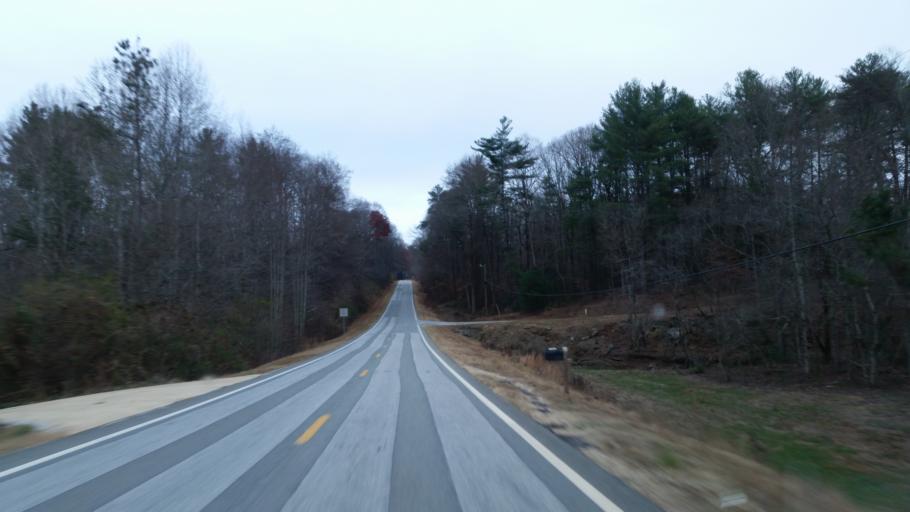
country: US
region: Georgia
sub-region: Dawson County
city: Dawsonville
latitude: 34.4959
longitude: -84.1969
